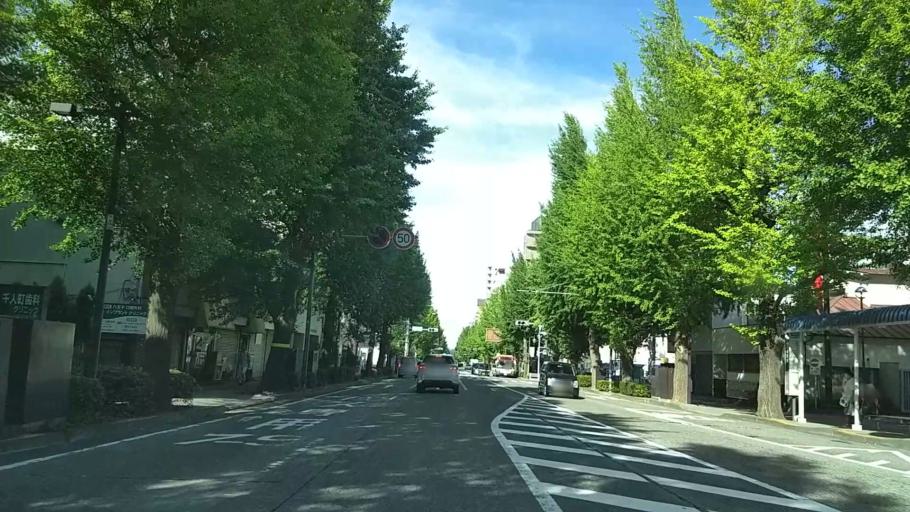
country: JP
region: Tokyo
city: Hachioji
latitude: 35.6571
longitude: 139.3108
